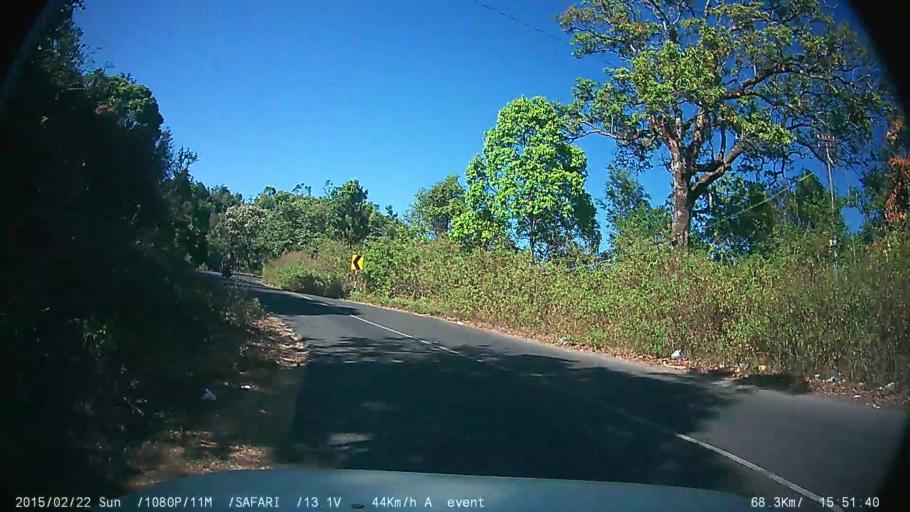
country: IN
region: Kerala
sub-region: Kottayam
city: Erattupetta
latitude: 9.5705
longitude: 77.0085
